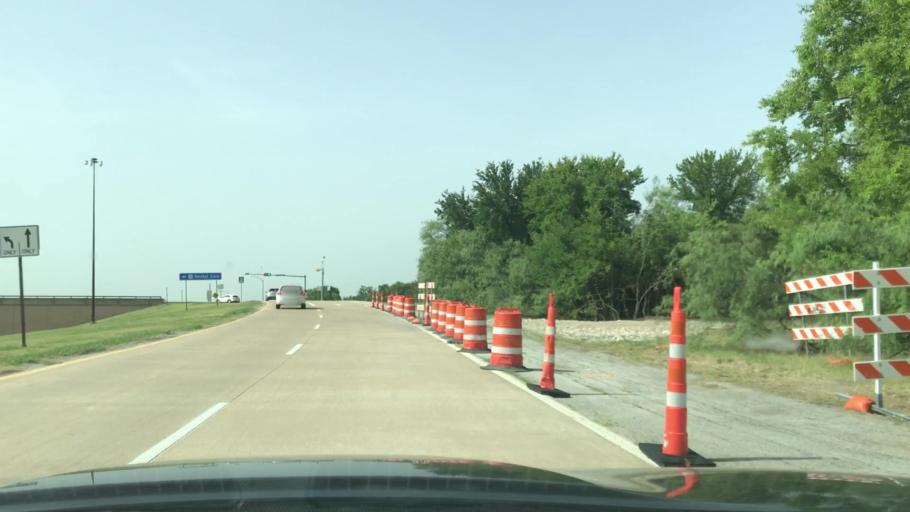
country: US
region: Texas
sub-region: Tarrant County
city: Euless
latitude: 32.8543
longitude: -97.0415
